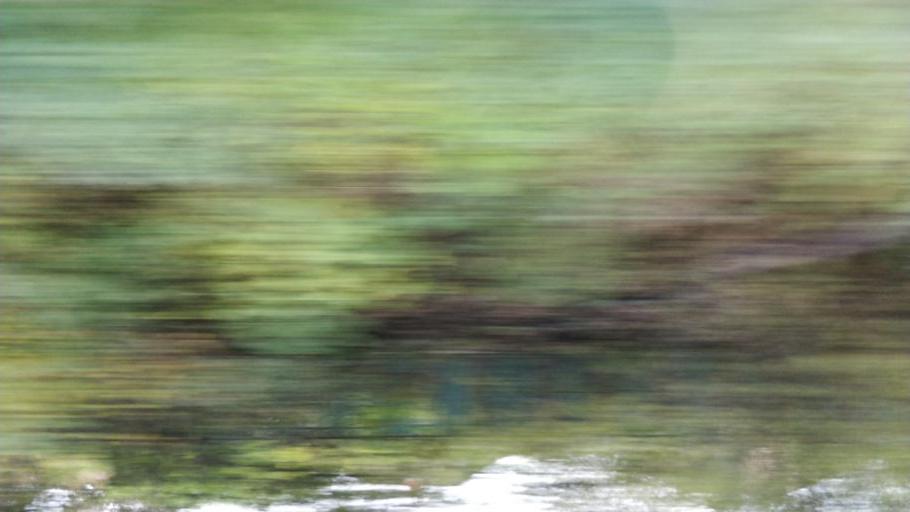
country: GB
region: England
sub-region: Borough of Bolton
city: Westhoughton
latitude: 53.5405
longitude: -2.5207
